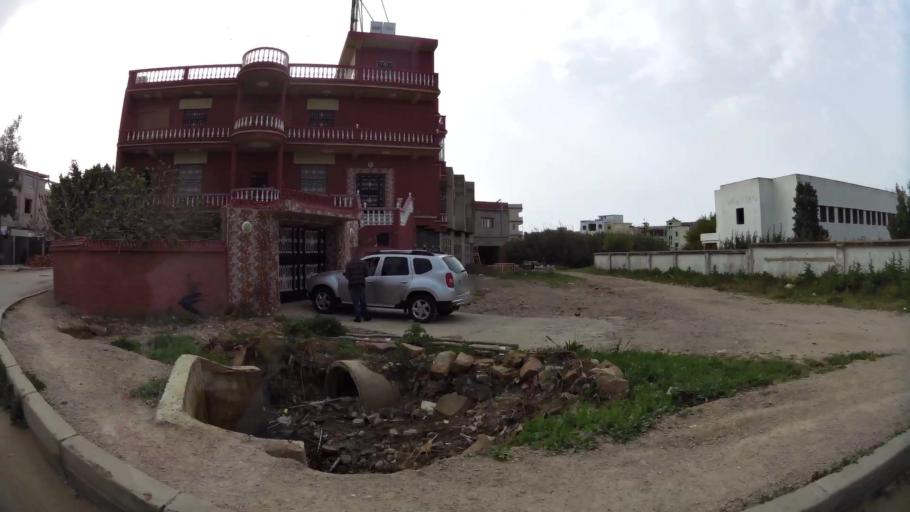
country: MA
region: Tanger-Tetouan
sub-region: Tanger-Assilah
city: Boukhalef
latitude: 35.7019
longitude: -5.8998
